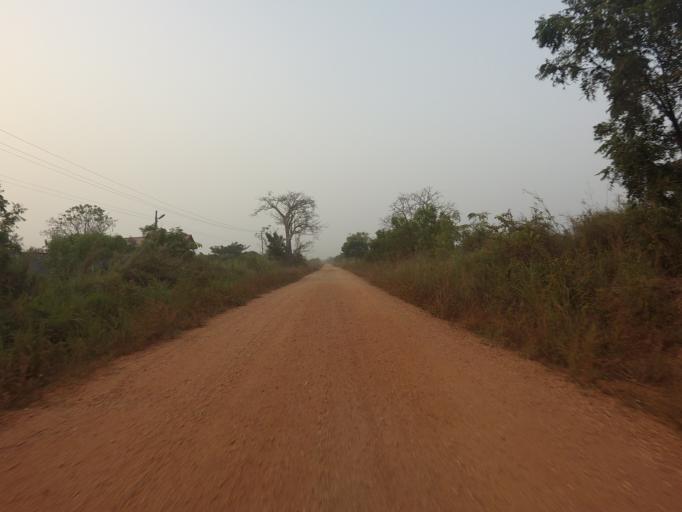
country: GH
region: Volta
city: Anloga
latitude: 5.9762
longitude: 0.6073
